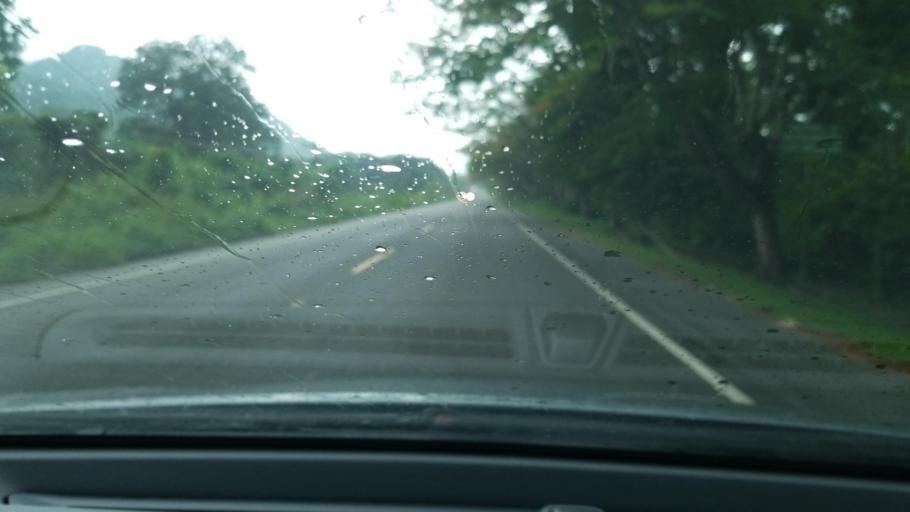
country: HN
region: Cortes
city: Rio Chiquito
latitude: 15.6208
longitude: -88.2672
